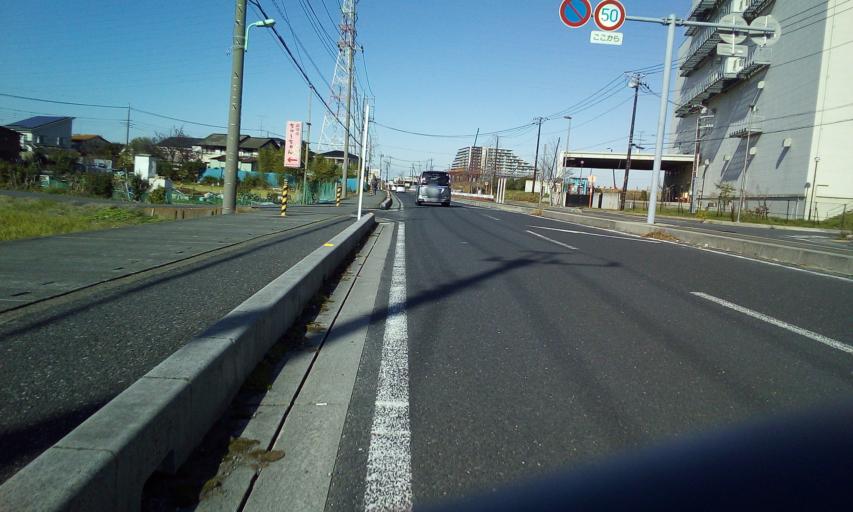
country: JP
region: Saitama
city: Yoshikawa
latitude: 35.8622
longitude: 139.8612
